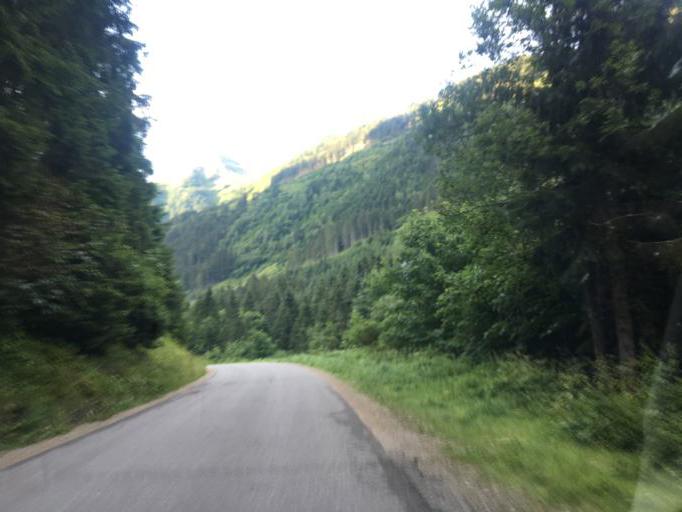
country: AT
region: Styria
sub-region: Politischer Bezirk Liezen
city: Schladming
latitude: 47.3461
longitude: 13.7309
